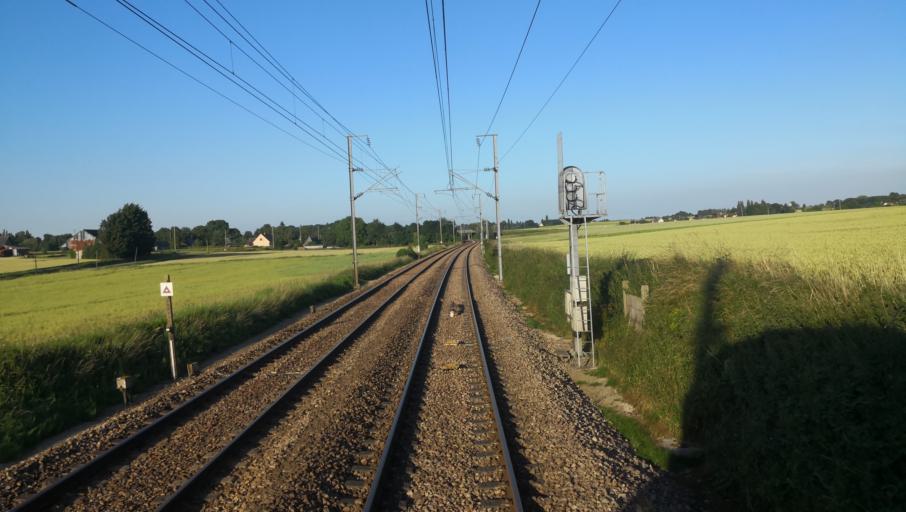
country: FR
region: Haute-Normandie
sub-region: Departement de l'Eure
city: Thiberville
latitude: 49.0808
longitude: 0.4948
